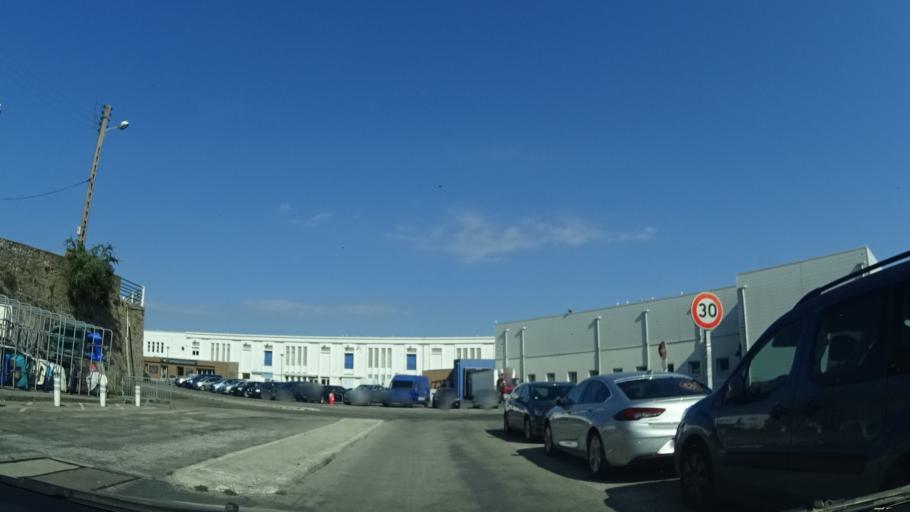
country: FR
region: Brittany
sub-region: Departement du Finistere
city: Douarnenez
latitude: 48.0968
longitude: -4.3244
